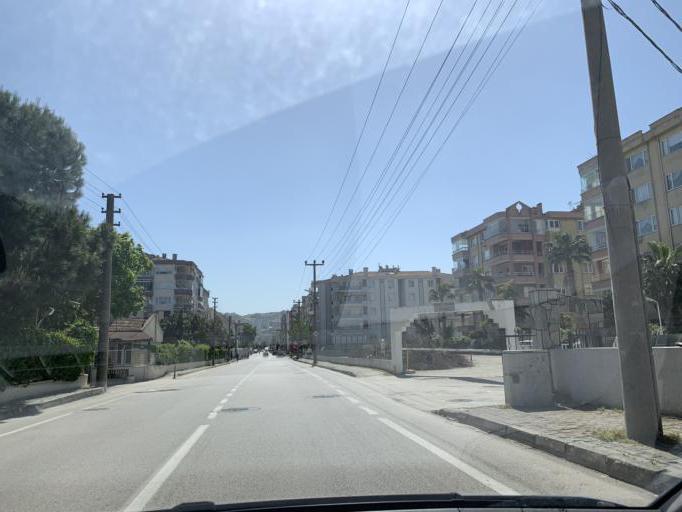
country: TR
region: Bursa
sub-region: Mudanya
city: Mudanya
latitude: 40.3579
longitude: 28.9166
